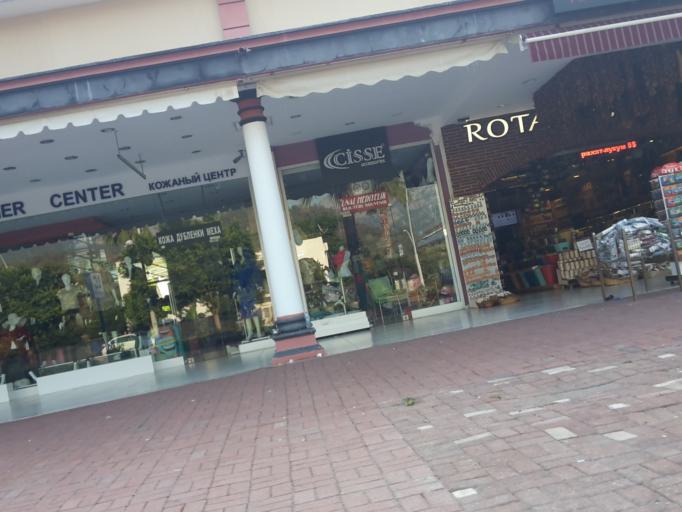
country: TR
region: Antalya
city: Kemer
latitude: 36.6072
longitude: 30.5587
